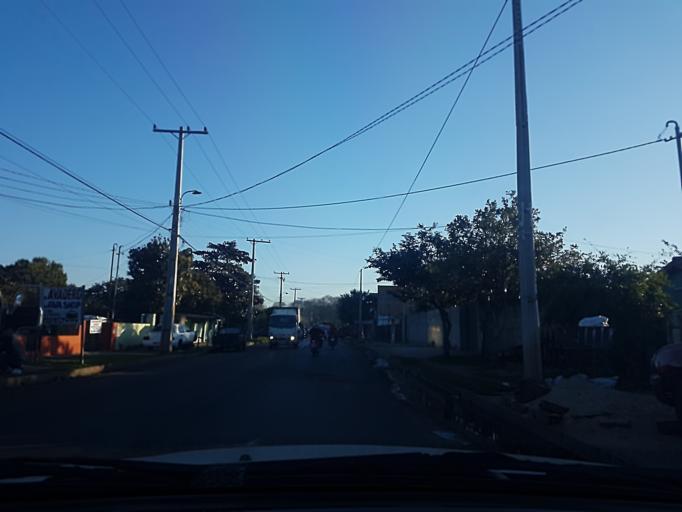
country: PY
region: Central
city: Colonia Mariano Roque Alonso
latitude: -25.2203
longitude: -57.5229
